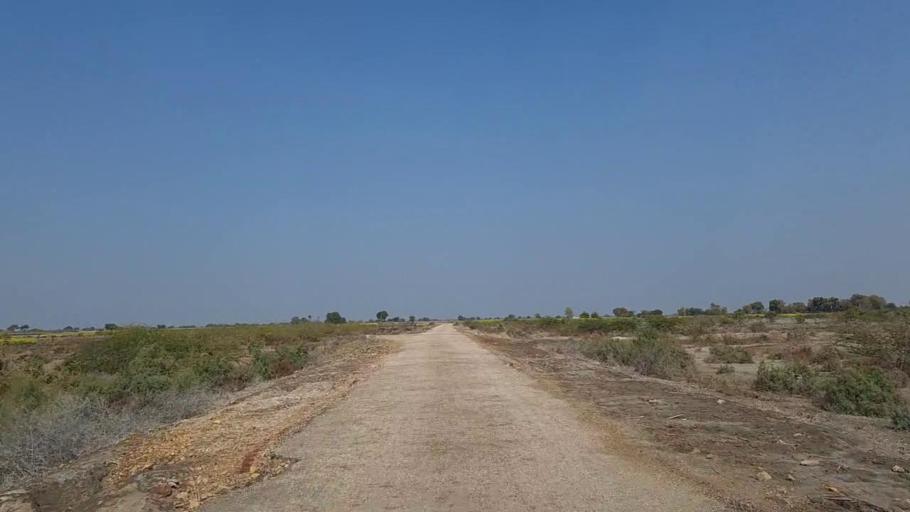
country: PK
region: Sindh
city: Nawabshah
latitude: 26.2918
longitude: 68.4810
